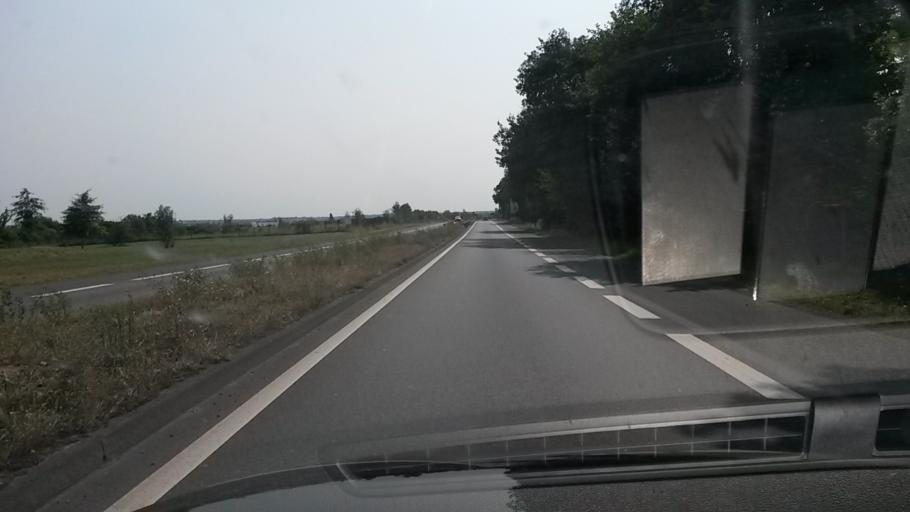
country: FR
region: Pays de la Loire
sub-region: Departement de la Loire-Atlantique
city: Saint-Gereon
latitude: 47.4081
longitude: -1.1900
